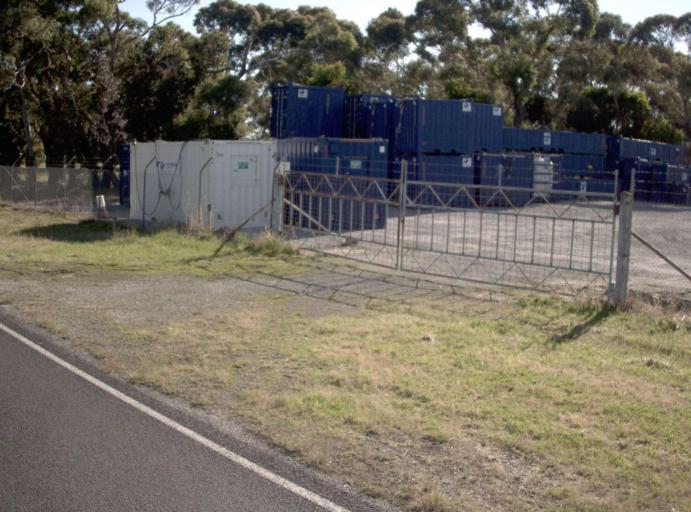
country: AU
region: Victoria
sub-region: Latrobe
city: Morwell
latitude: -38.6969
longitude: 146.3996
